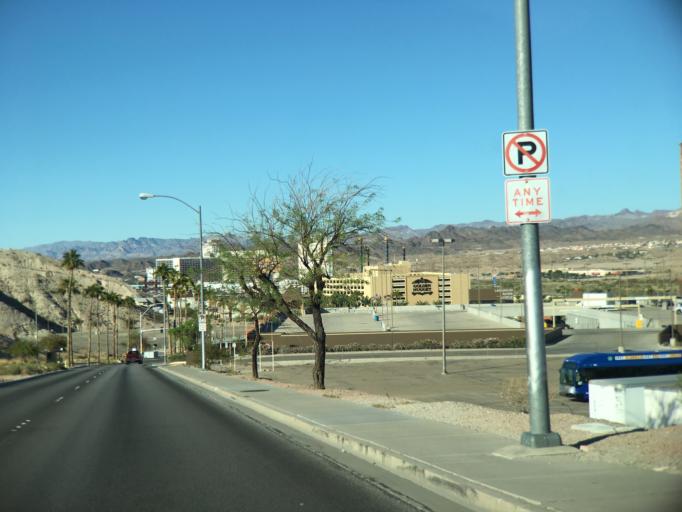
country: US
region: Arizona
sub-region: Mohave County
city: Bullhead City
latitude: 35.1480
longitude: -114.5771
